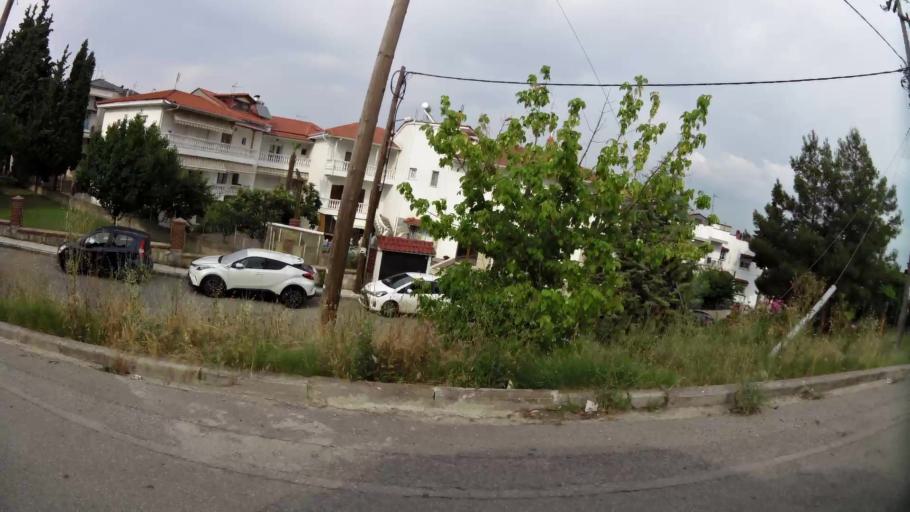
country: GR
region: Central Macedonia
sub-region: Nomos Thessalonikis
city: Oraiokastro
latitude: 40.7357
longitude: 22.9186
